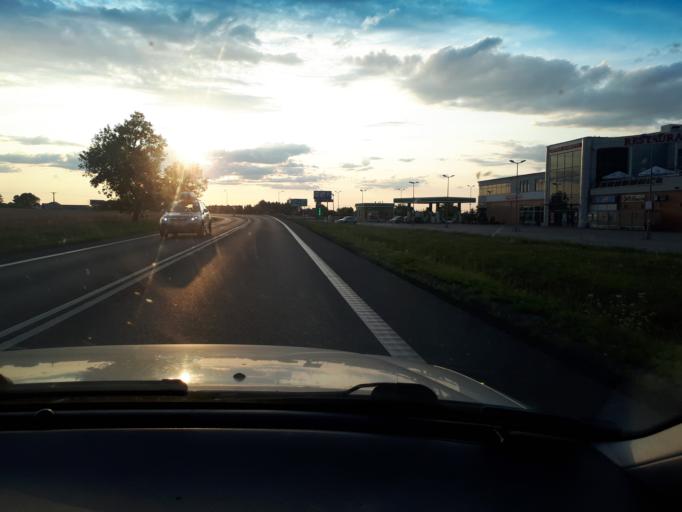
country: PL
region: Subcarpathian Voivodeship
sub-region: Powiat ropczycko-sedziszowski
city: Sedziszow Malopolski
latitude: 50.0677
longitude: 21.6804
